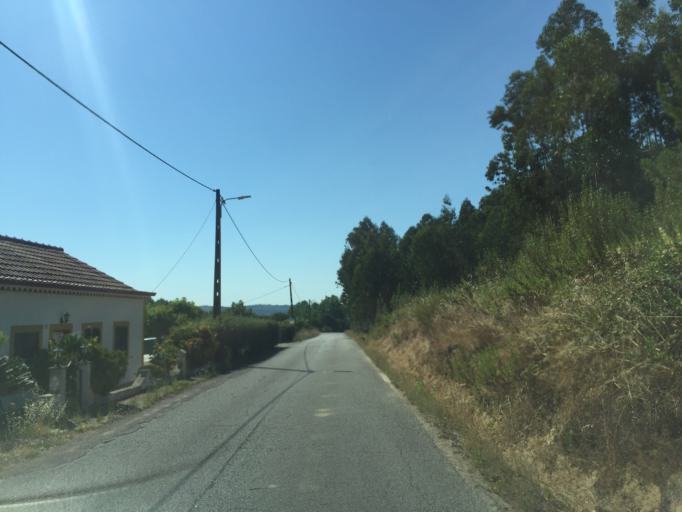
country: PT
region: Santarem
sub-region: Constancia
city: Constancia
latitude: 39.5590
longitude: -8.3188
